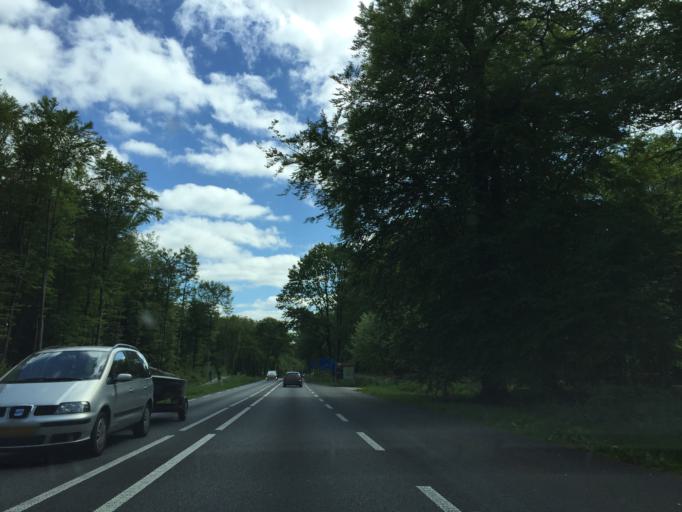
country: NL
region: Gelderland
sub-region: Gemeente Apeldoorn
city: Apeldoorn
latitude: 52.2302
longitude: 5.8973
